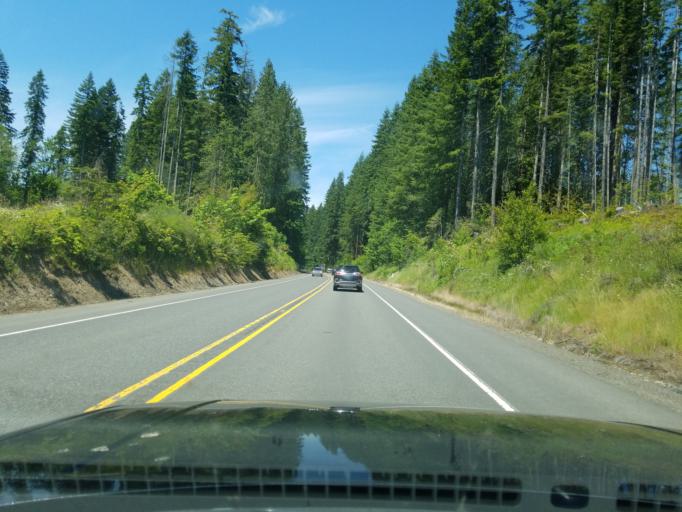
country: US
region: Oregon
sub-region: Columbia County
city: Vernonia
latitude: 45.7719
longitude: -123.3225
